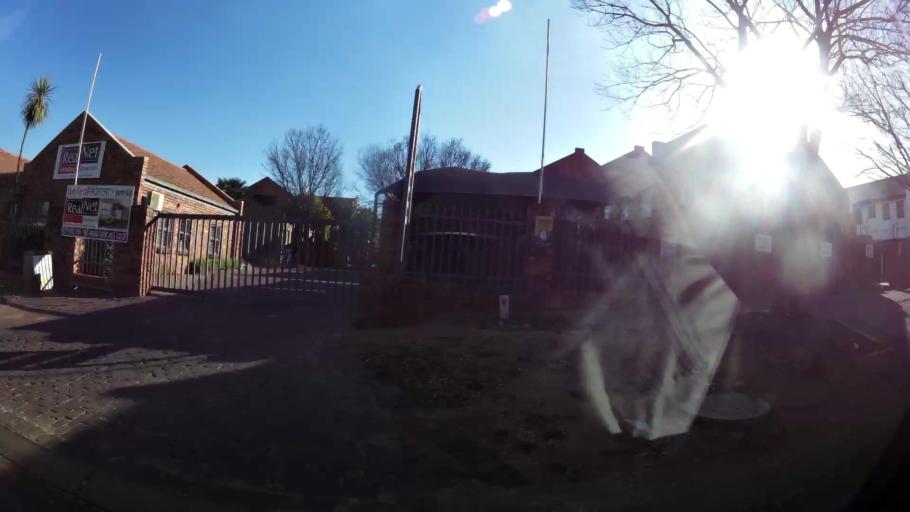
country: ZA
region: Gauteng
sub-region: City of Johannesburg Metropolitan Municipality
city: Roodepoort
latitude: -26.0866
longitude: 27.9618
